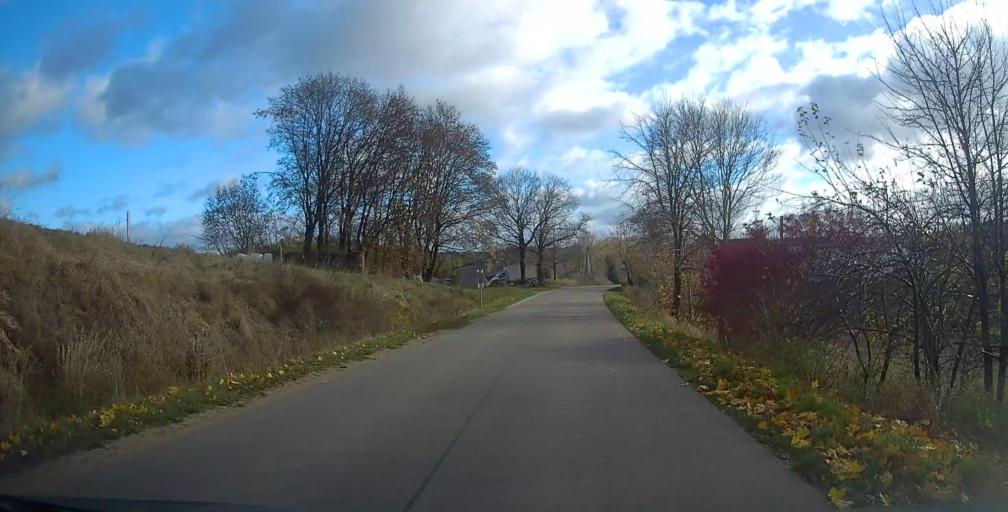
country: PL
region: Podlasie
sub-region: Suwalki
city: Suwalki
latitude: 54.2829
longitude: 22.9035
